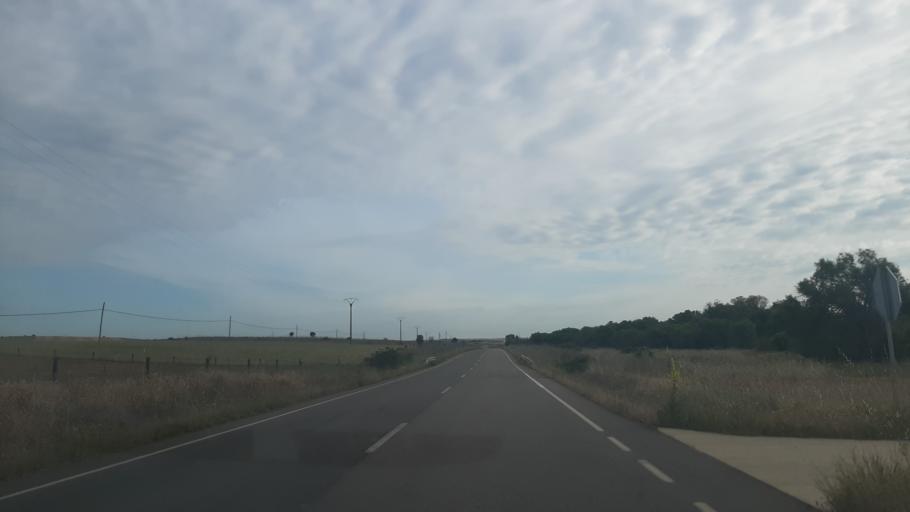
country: ES
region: Castille and Leon
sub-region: Provincia de Salamanca
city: Gallegos de Arganan
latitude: 40.6119
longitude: -6.7064
